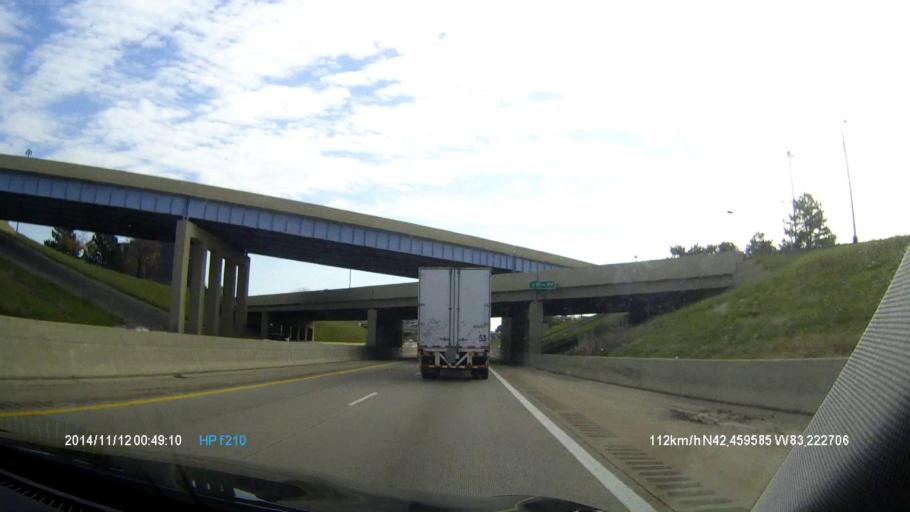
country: US
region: Michigan
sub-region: Oakland County
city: Southfield
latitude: 42.4594
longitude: -83.2225
